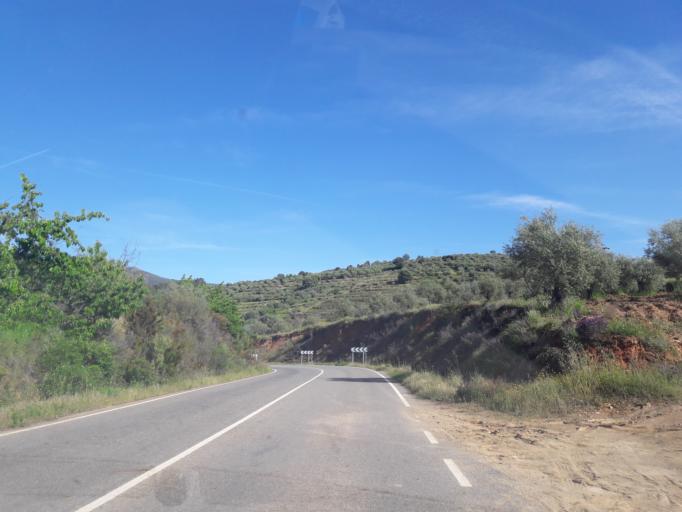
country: ES
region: Castille and Leon
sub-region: Provincia de Salamanca
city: Sotoserrano
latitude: 40.4251
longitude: -6.0362
